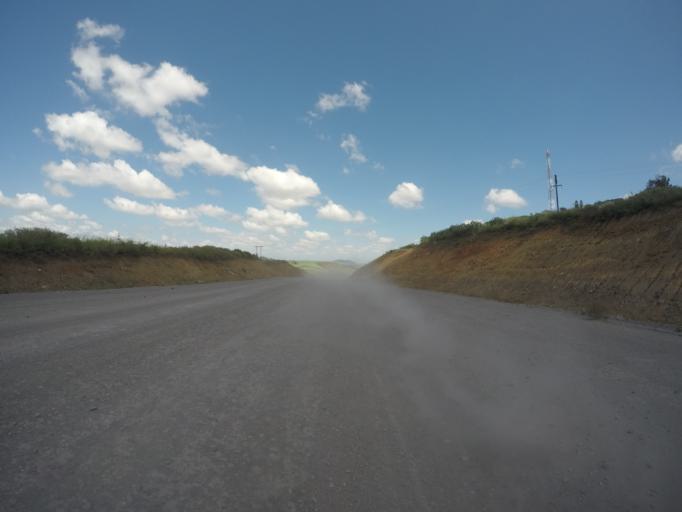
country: ZA
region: KwaZulu-Natal
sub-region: uThungulu District Municipality
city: Empangeni
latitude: -28.6326
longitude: 31.7613
